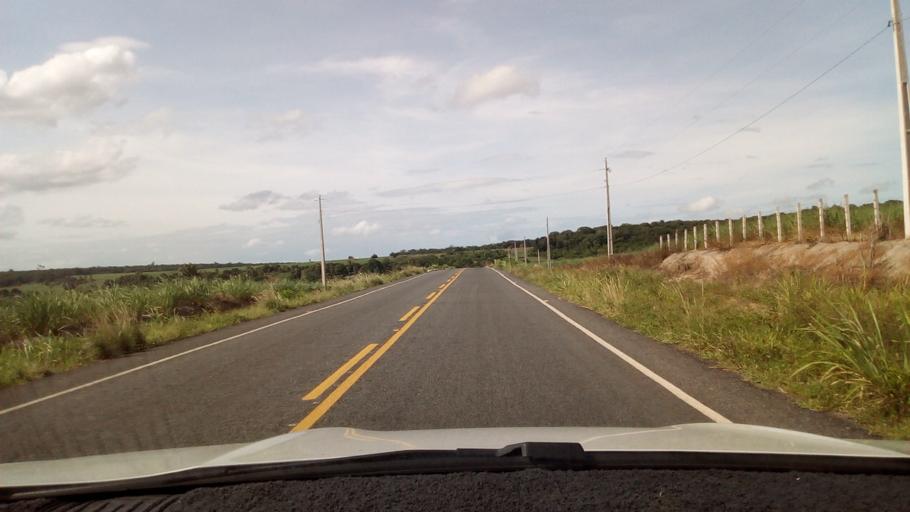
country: BR
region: Paraiba
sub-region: Santa Rita
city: Santa Rita
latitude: -7.0644
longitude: -34.9541
